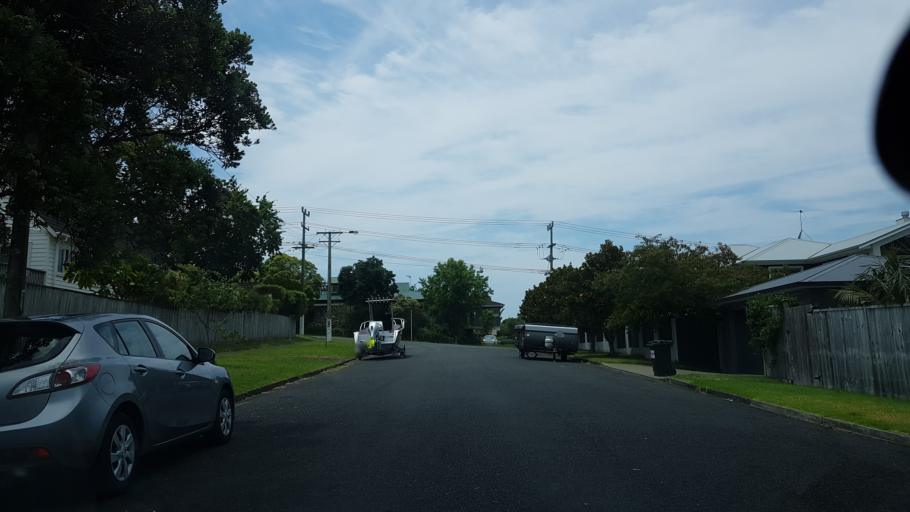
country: NZ
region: Auckland
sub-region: Auckland
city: North Shore
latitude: -36.8006
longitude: 174.7783
